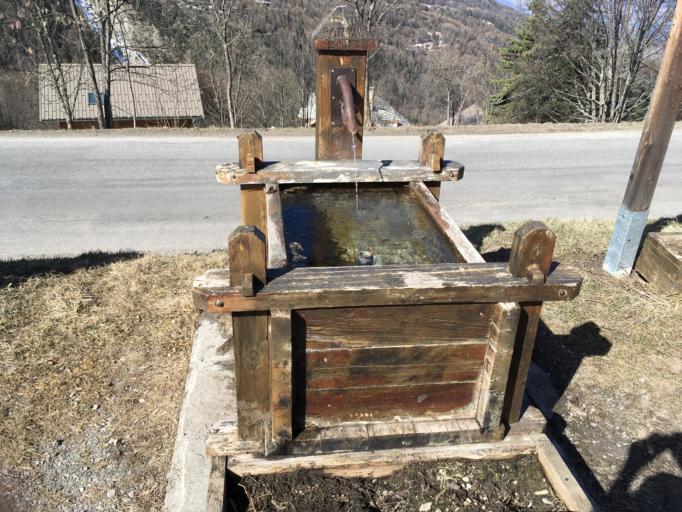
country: FR
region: Provence-Alpes-Cote d'Azur
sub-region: Departement des Hautes-Alpes
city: Embrun
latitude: 44.4988
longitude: 6.5554
